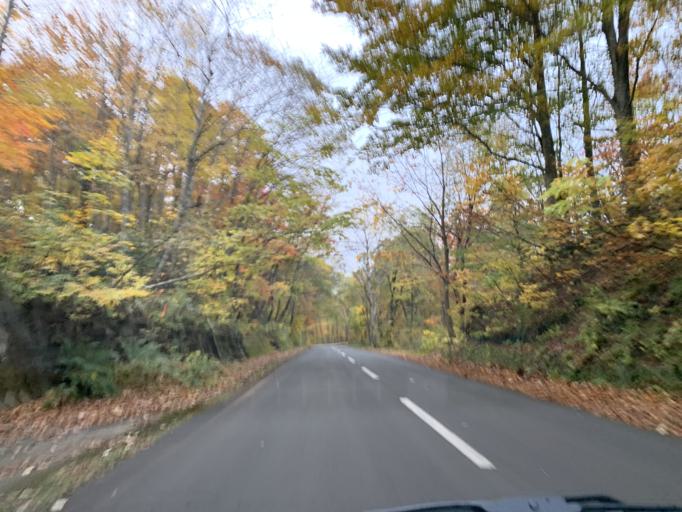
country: JP
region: Iwate
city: Mizusawa
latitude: 39.1056
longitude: 140.8627
